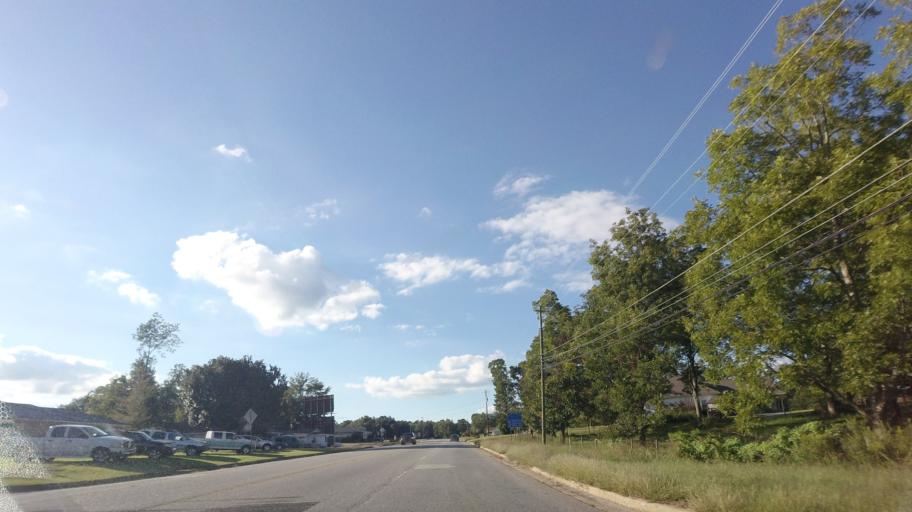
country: US
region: Georgia
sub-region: Upson County
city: Hannahs Mill
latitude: 32.9443
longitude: -84.3353
